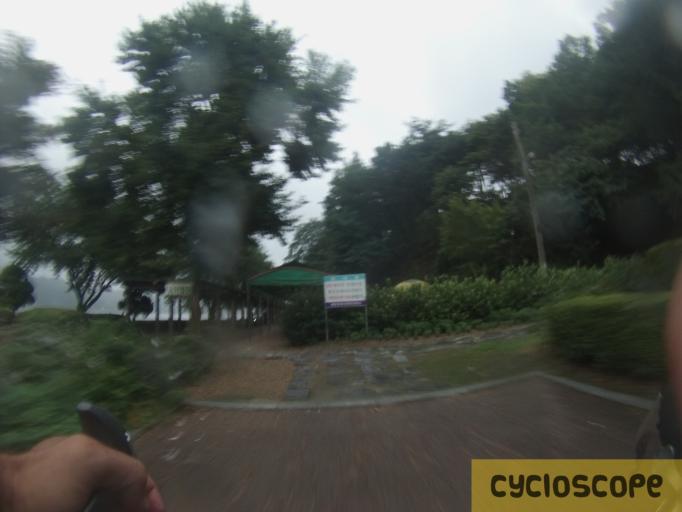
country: KR
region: Chungcheongnam-do
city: Yesan
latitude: 36.7283
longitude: 126.8552
